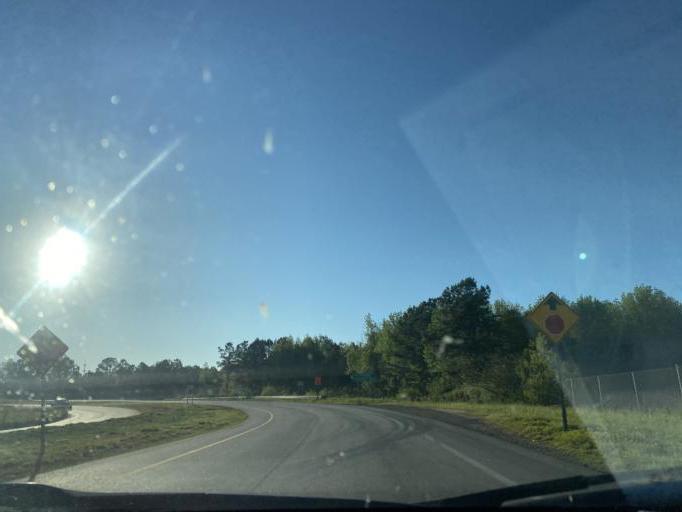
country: US
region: South Carolina
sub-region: Spartanburg County
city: Mayo
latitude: 35.0279
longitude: -81.8748
